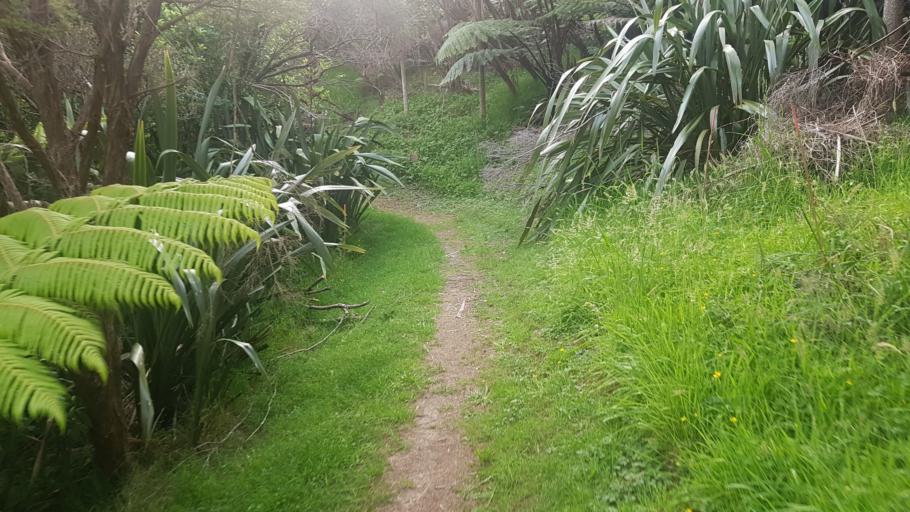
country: NZ
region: Auckland
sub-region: Auckland
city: Pakuranga
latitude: -36.7796
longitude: 175.0012
